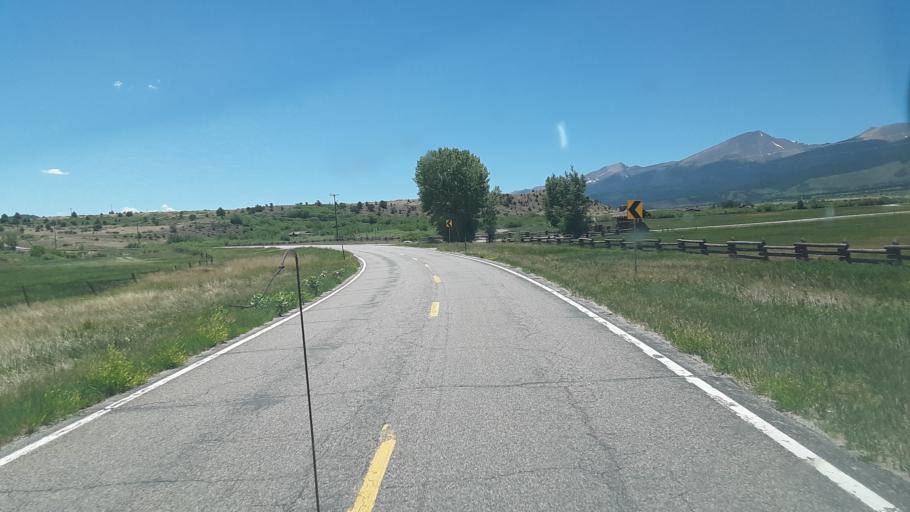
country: US
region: Colorado
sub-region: Custer County
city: Westcliffe
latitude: 38.2908
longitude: -105.6208
